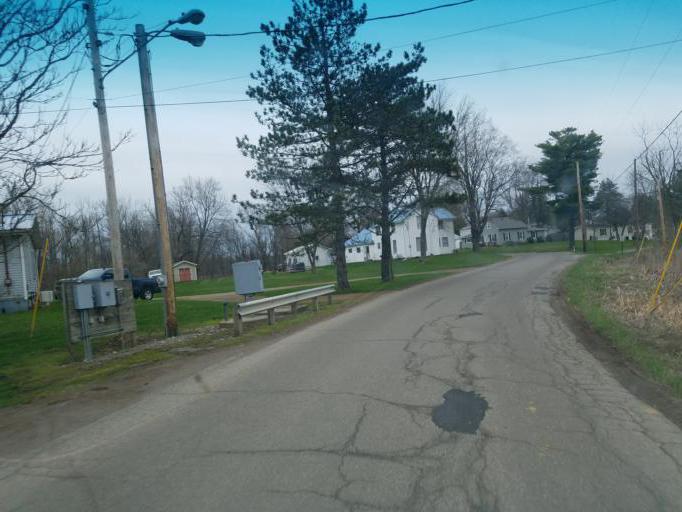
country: US
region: Ohio
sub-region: Holmes County
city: Millersburg
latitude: 40.6286
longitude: -81.9286
